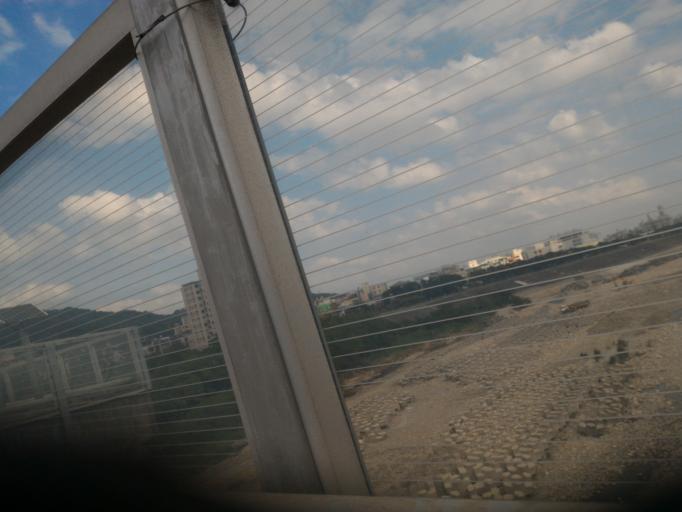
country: TW
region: Taiwan
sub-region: Taoyuan
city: Taoyuan
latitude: 24.9667
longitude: 121.3943
